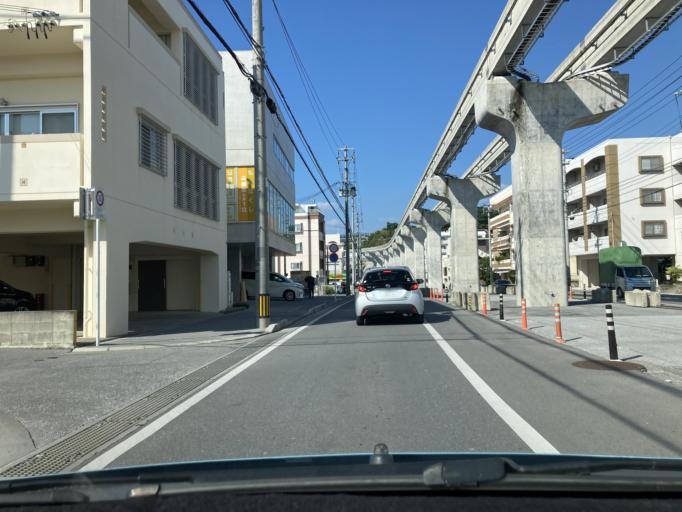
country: JP
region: Okinawa
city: Ginowan
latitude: 26.2320
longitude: 127.7288
